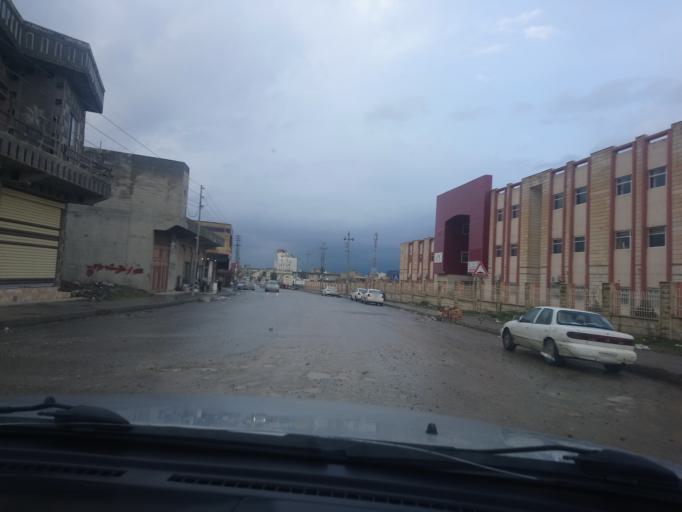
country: IQ
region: As Sulaymaniyah
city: Qeladize
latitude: 36.1814
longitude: 45.1371
